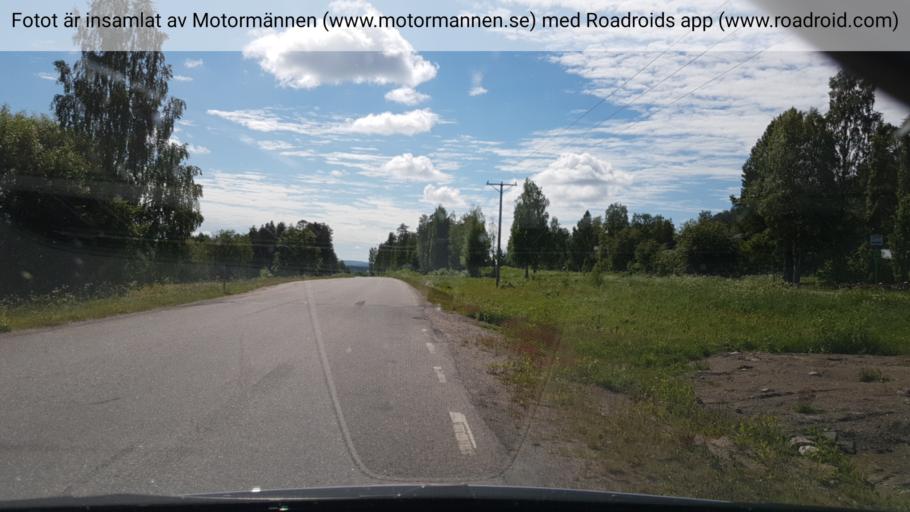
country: FI
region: Lapland
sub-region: Torniolaakso
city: Pello
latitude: 66.6566
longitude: 23.8561
